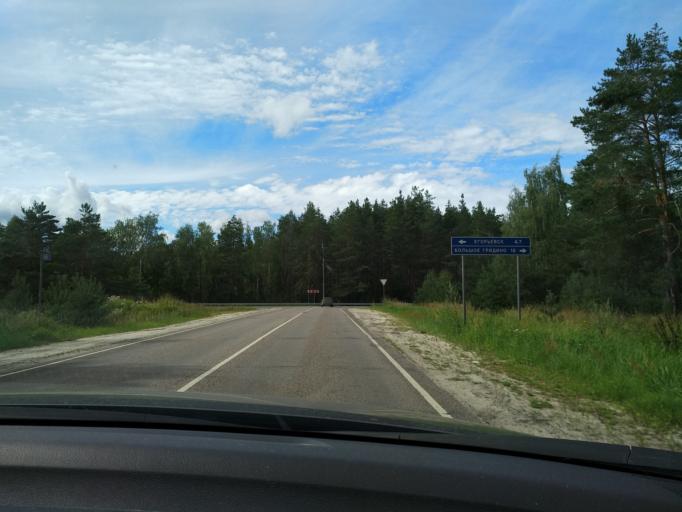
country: RU
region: Moskovskaya
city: Krasnyy Tkach
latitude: 55.3992
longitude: 39.1316
